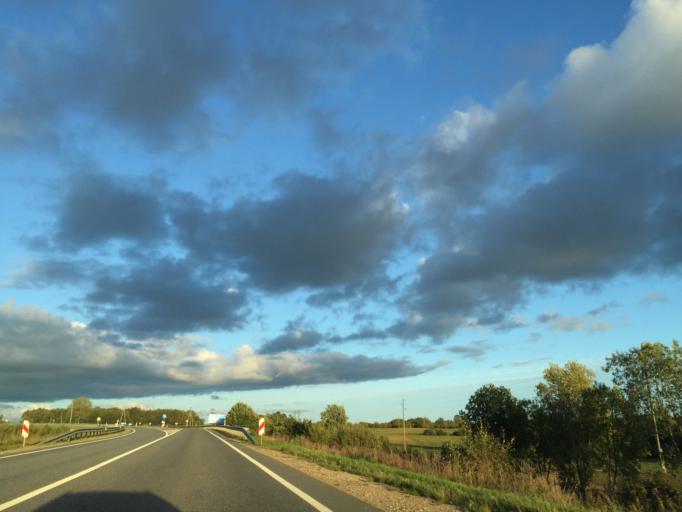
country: LV
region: Broceni
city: Broceni
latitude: 56.6894
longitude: 22.5482
